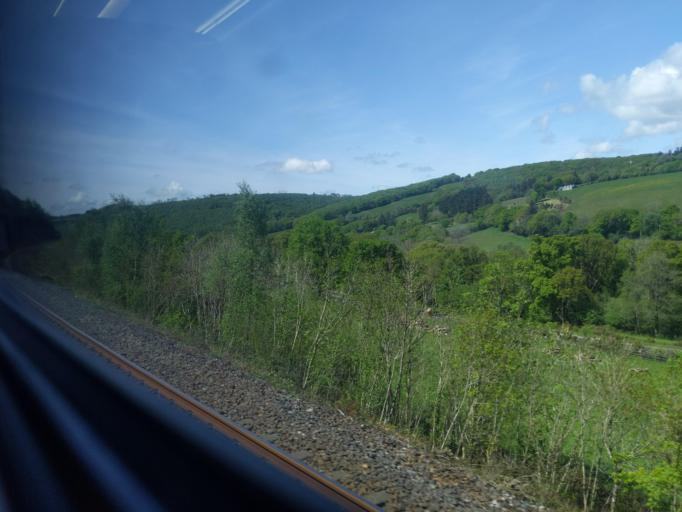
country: GB
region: England
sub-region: Cornwall
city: Lostwithiel
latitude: 50.4561
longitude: -4.6055
